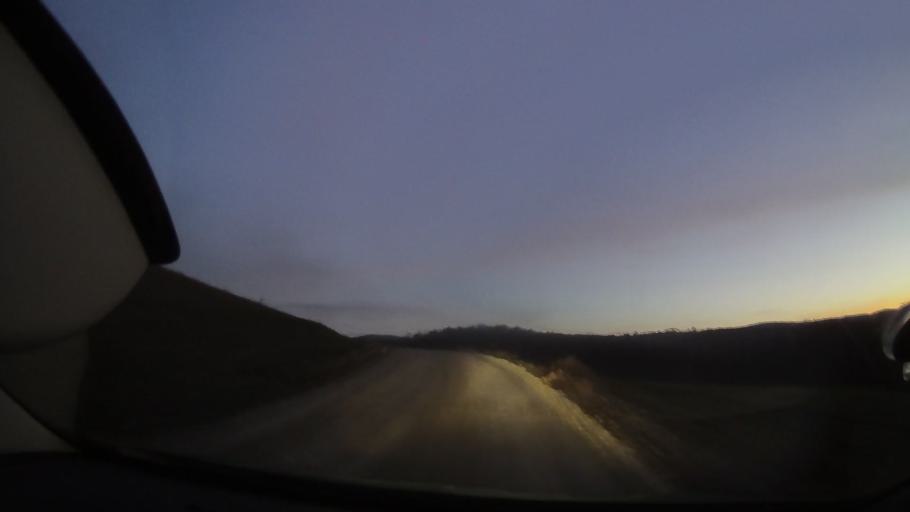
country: RO
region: Bihor
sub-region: Comuna Tetchea
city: Hotar
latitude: 47.0087
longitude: 22.3064
